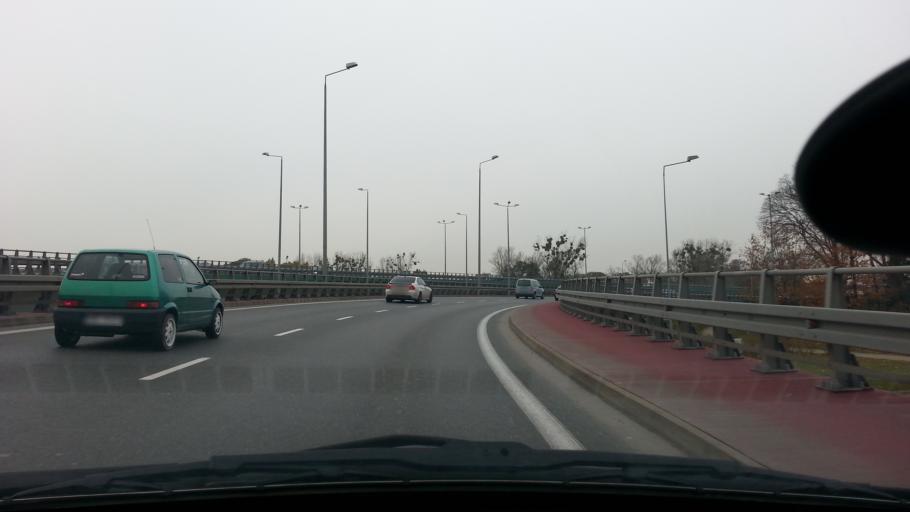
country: PL
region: Masovian Voivodeship
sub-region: Warszawa
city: Zoliborz
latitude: 52.2558
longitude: 20.9495
